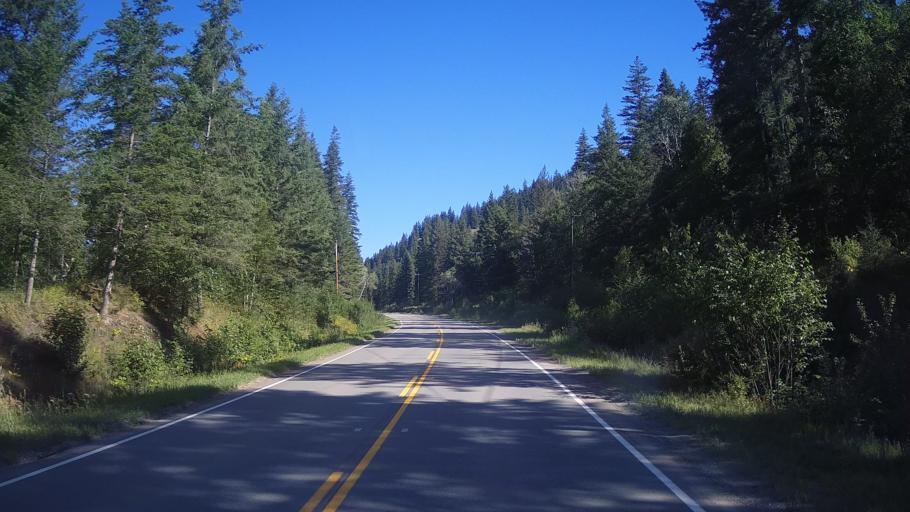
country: CA
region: British Columbia
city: Kamloops
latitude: 51.4461
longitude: -120.2124
